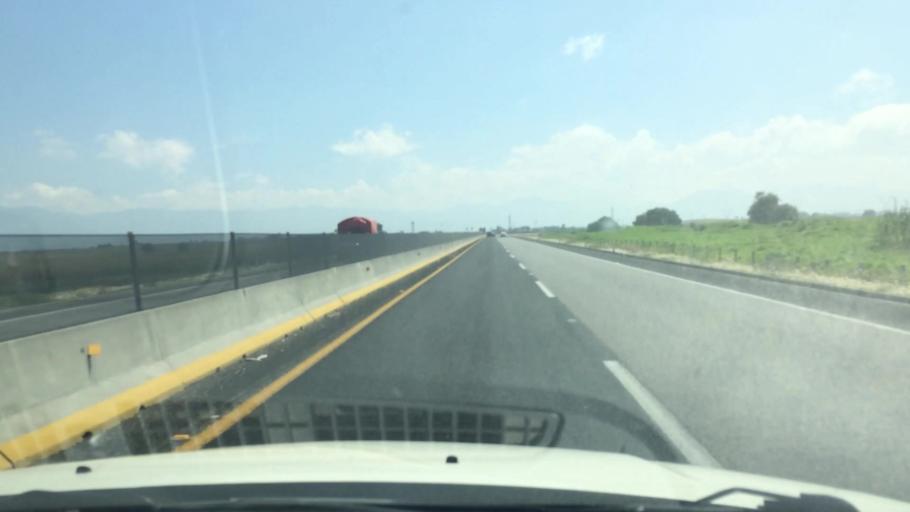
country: MX
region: Mexico
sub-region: Temoaya
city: Llano de la Y
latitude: 19.4066
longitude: -99.6025
